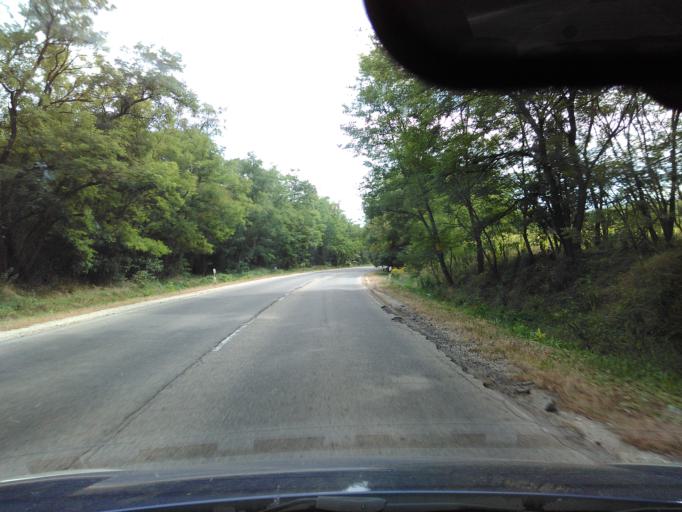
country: HU
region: Pest
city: Godollo
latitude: 47.6083
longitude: 19.4072
